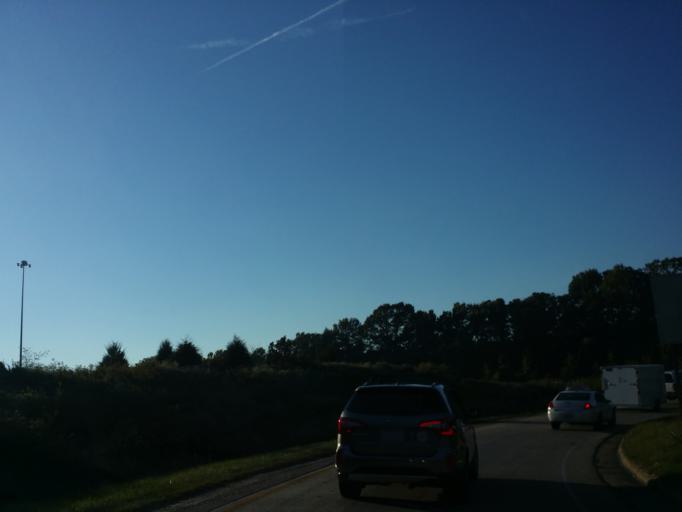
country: US
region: North Carolina
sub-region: Wake County
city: Cary
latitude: 35.7606
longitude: -78.7458
